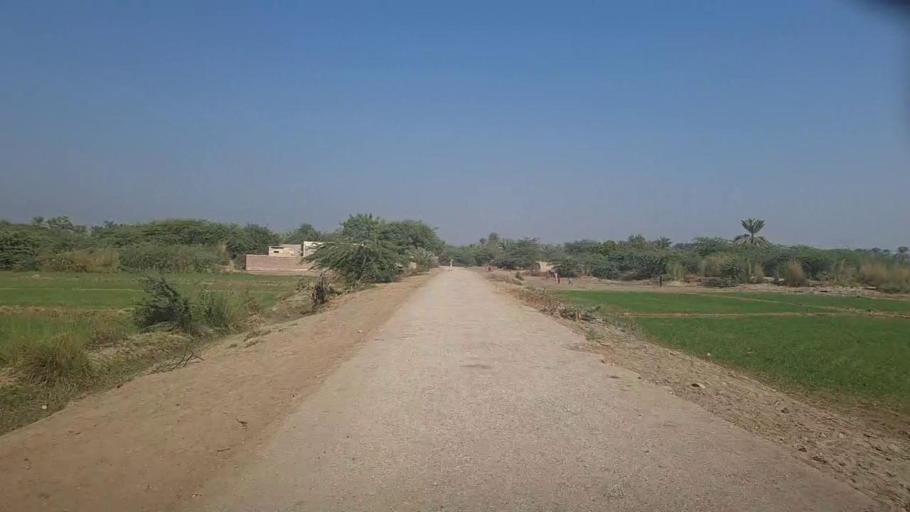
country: PK
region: Sindh
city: Kot Diji
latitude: 27.4165
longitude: 68.7056
